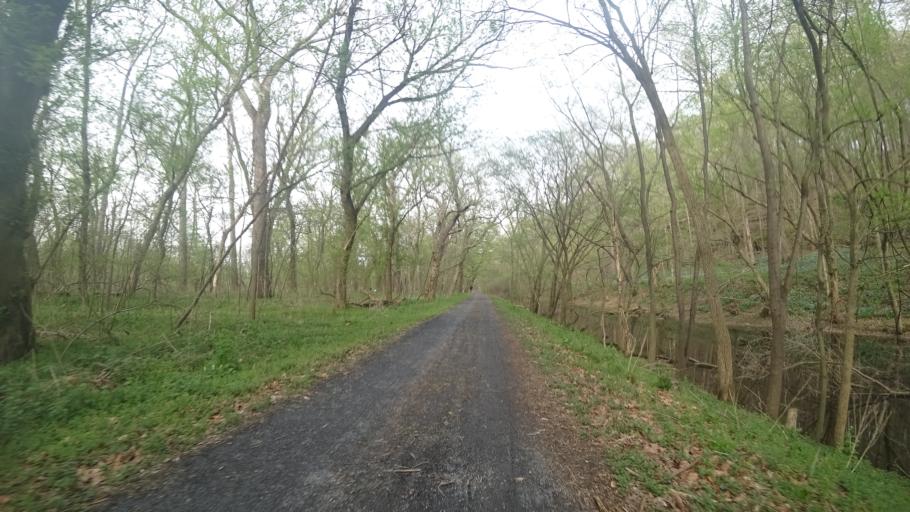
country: US
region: Maryland
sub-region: Montgomery County
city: Poolesville
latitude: 39.1789
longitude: -77.4934
